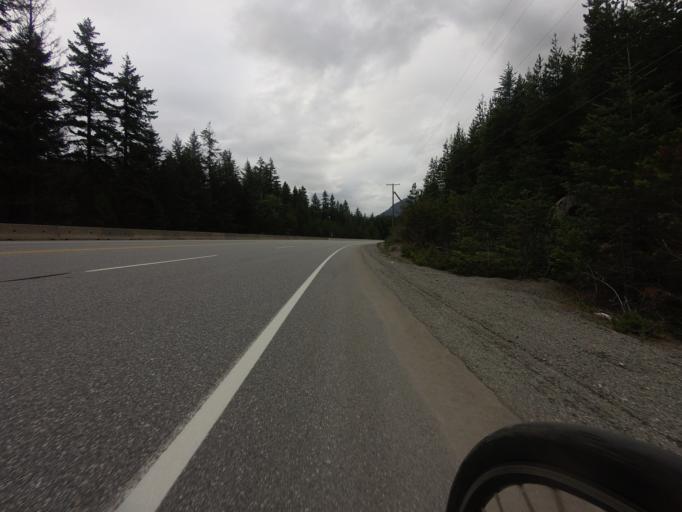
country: CA
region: British Columbia
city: Pemberton
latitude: 50.2185
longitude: -122.8850
